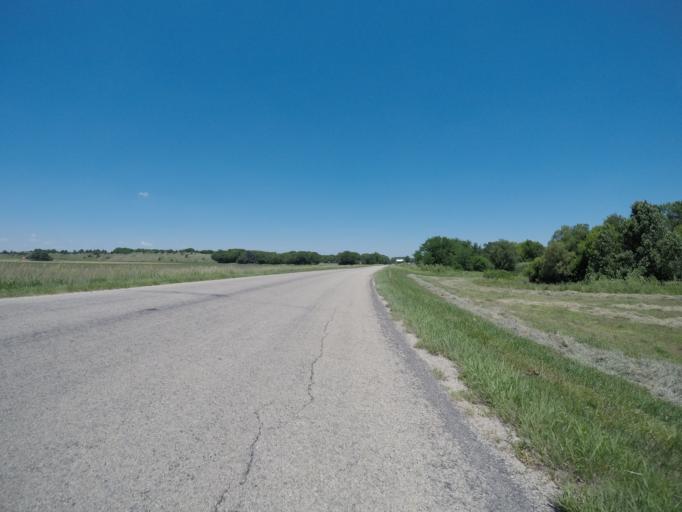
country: US
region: Kansas
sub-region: Geary County
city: Grandview Plaza
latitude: 38.8631
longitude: -96.7924
